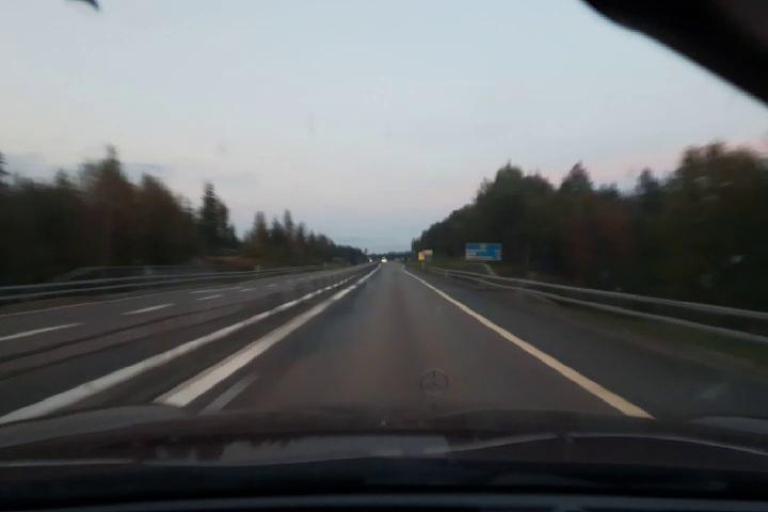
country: SE
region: Vaesternorrland
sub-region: Kramfors Kommun
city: Nordingra
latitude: 62.8770
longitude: 18.0679
